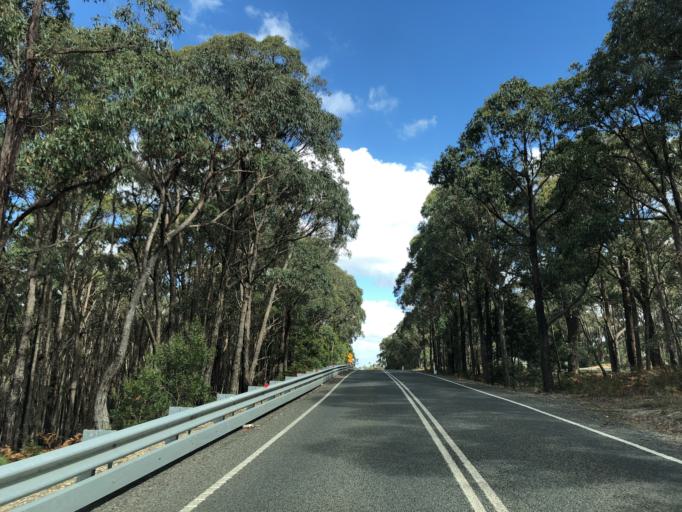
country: AU
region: Victoria
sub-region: Moorabool
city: Bacchus Marsh
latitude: -37.5059
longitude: 144.3107
